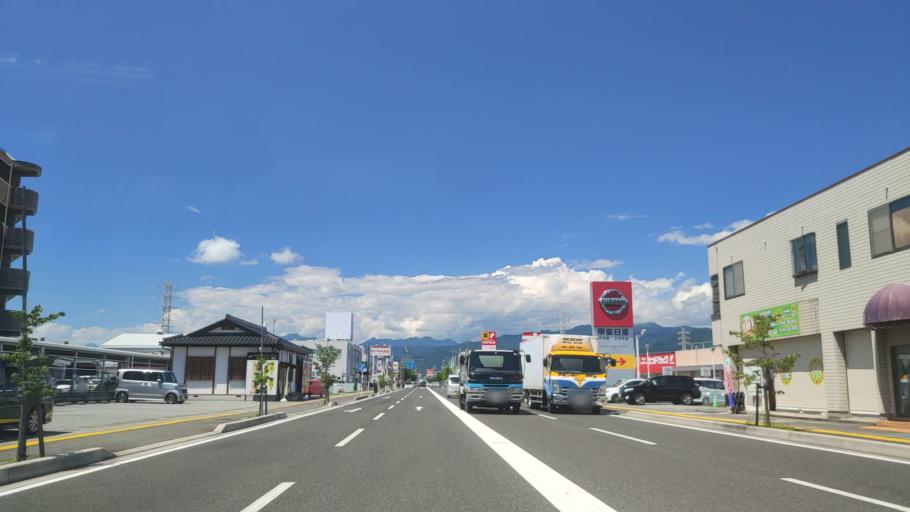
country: JP
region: Yamanashi
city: Kofu-shi
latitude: 35.6239
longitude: 138.5720
